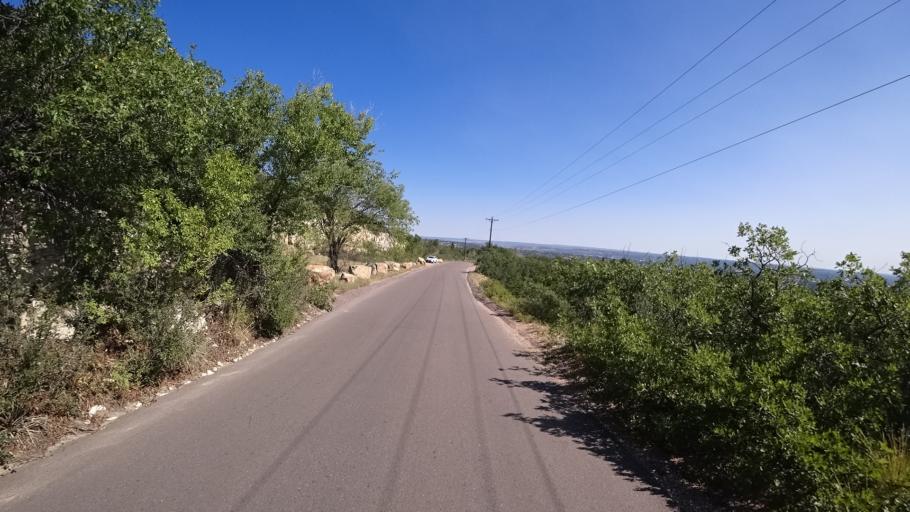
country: US
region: Colorado
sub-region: El Paso County
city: Manitou Springs
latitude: 38.8292
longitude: -104.8820
